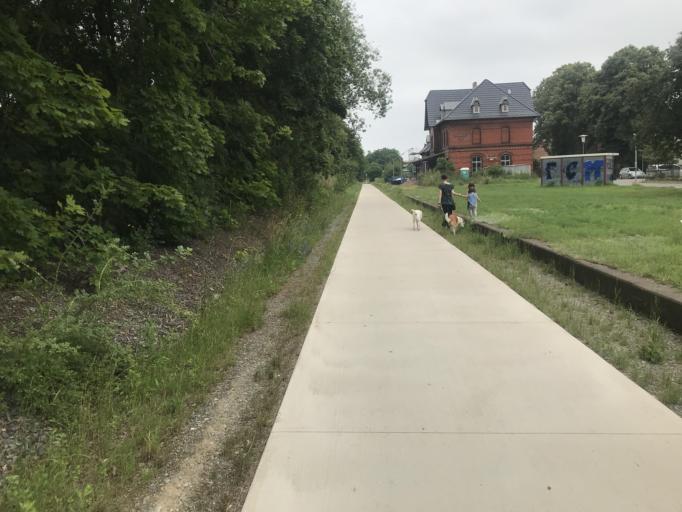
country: DE
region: Saxony-Anhalt
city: Ballenstedt
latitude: 51.7245
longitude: 11.2240
